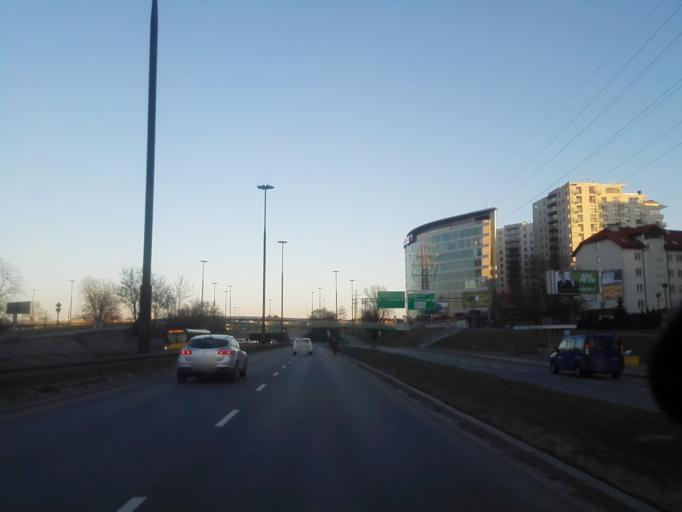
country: PL
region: Masovian Voivodeship
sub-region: Warszawa
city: Mokotow
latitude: 52.1681
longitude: 21.0130
